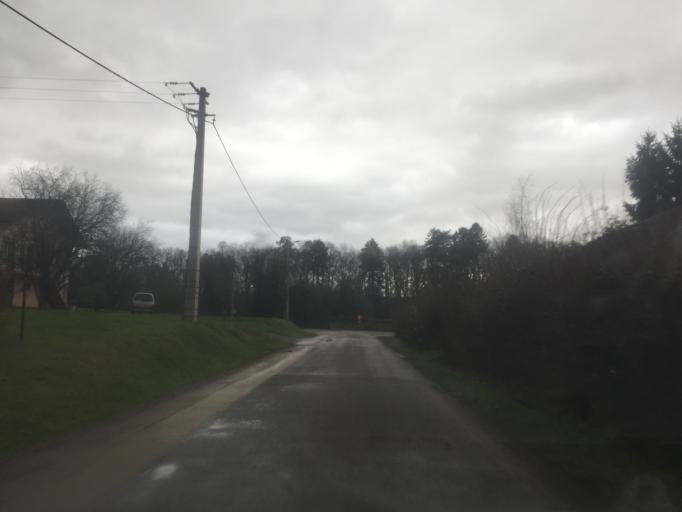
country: FR
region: Franche-Comte
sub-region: Departement du Jura
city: Orchamps
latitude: 47.2242
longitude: 5.6819
